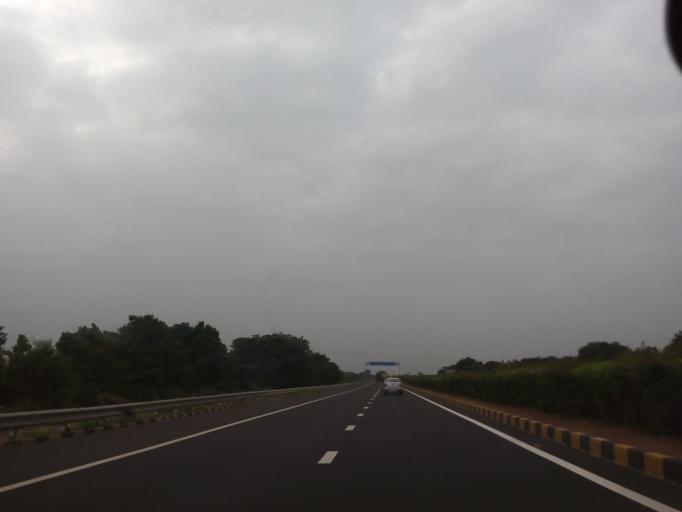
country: IN
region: Gujarat
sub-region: Kheda
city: Chaklasi
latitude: 22.6070
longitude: 72.9719
